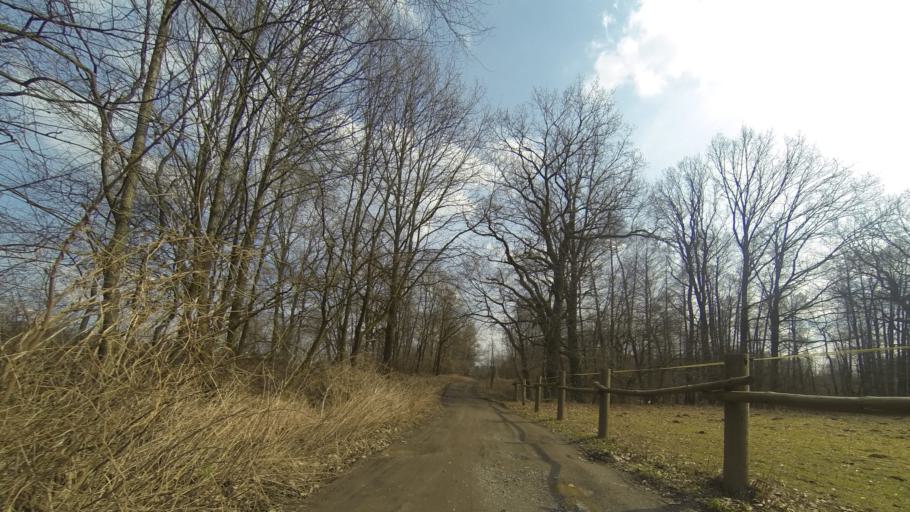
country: DE
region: Saxony
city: Radeburg
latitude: 51.2263
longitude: 13.7134
